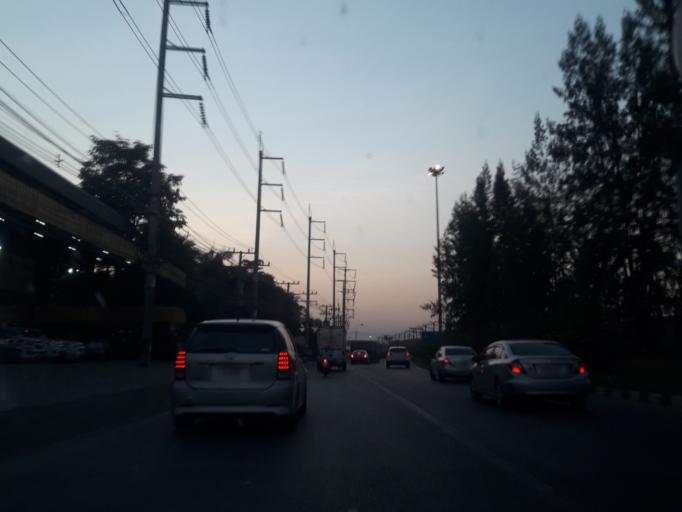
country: TH
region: Pathum Thani
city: Thanyaburi
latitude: 14.0669
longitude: 100.7039
